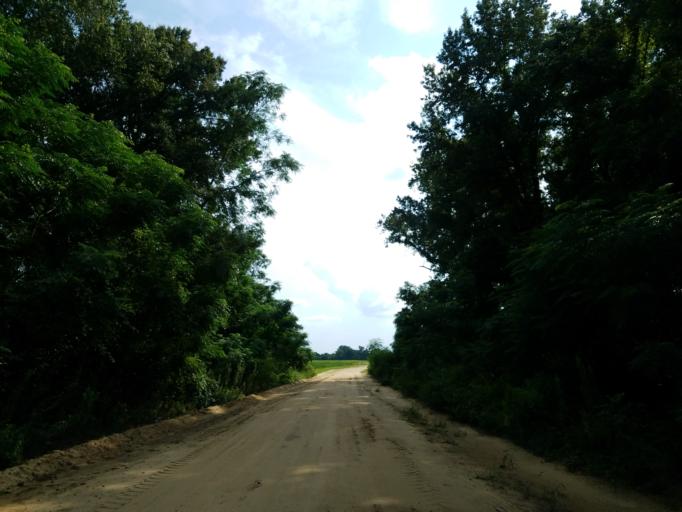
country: US
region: Georgia
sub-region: Dooly County
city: Unadilla
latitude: 32.1875
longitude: -83.7415
